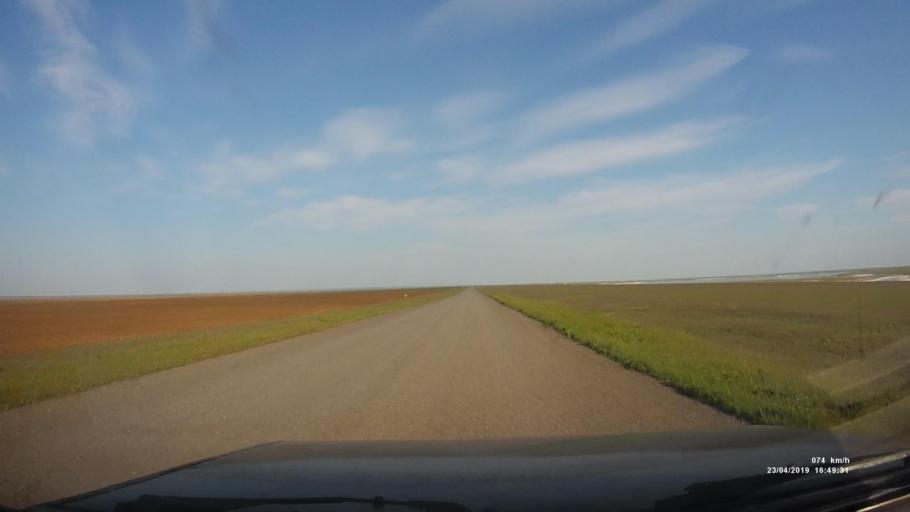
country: RU
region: Kalmykiya
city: Priyutnoye
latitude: 46.3306
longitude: 43.2778
